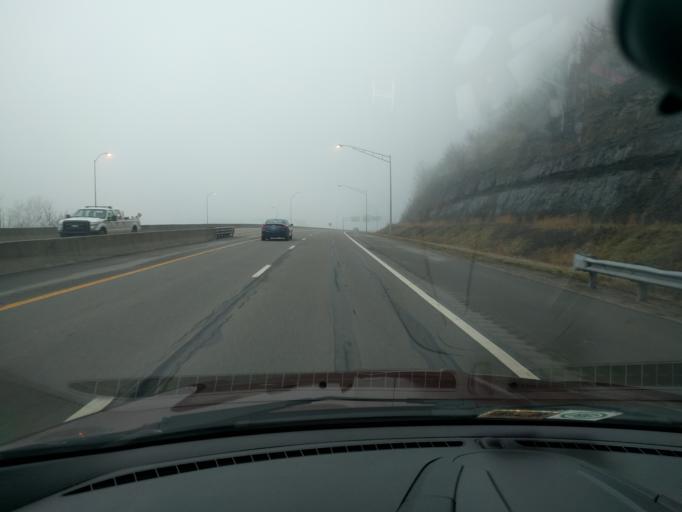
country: US
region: West Virginia
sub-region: Kanawha County
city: Chesapeake
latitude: 38.2000
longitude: -81.4915
